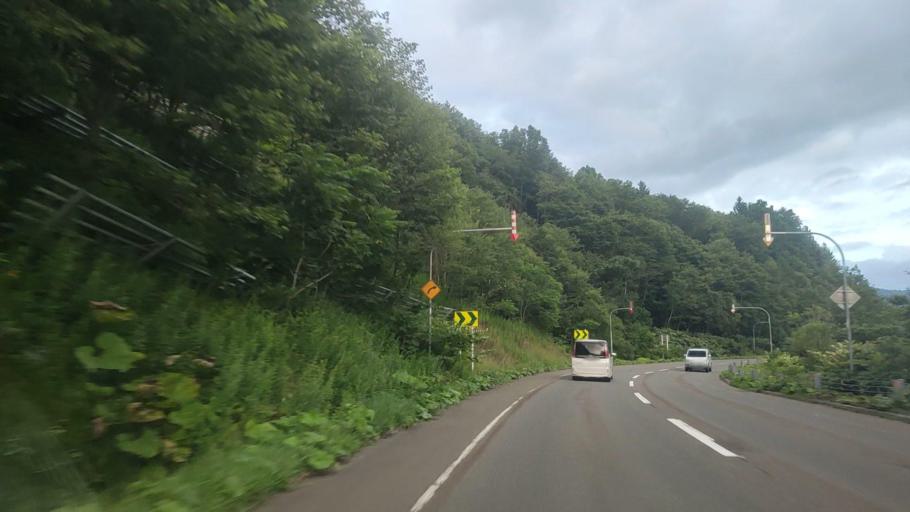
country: JP
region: Hokkaido
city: Shimo-furano
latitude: 43.3609
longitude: 142.2422
